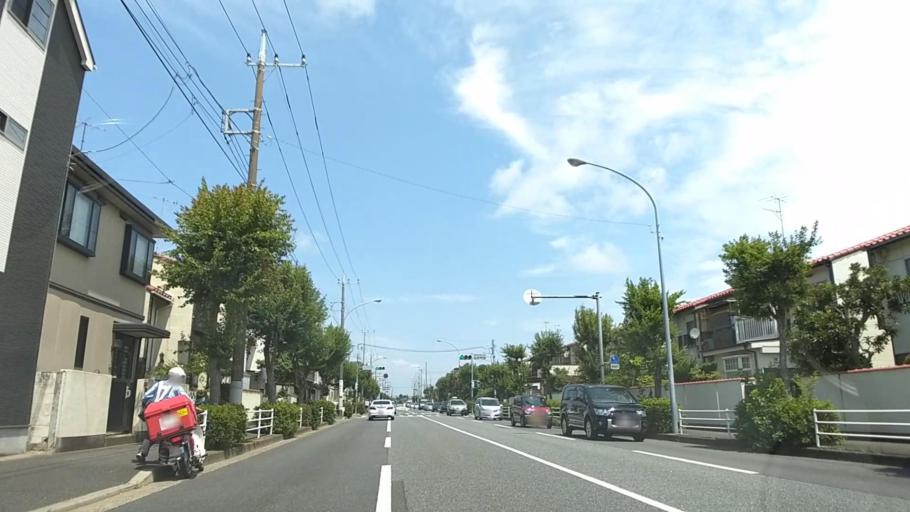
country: JP
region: Kanagawa
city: Minami-rinkan
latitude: 35.4446
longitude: 139.4843
